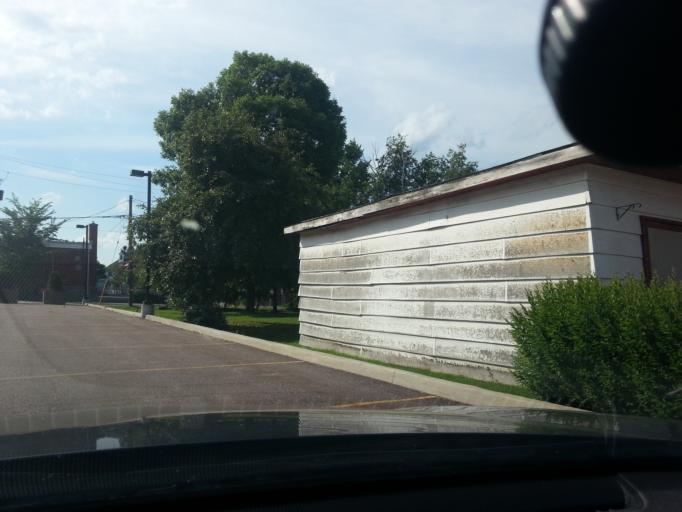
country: CA
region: Ontario
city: Arnprior
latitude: 45.4341
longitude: -76.3523
